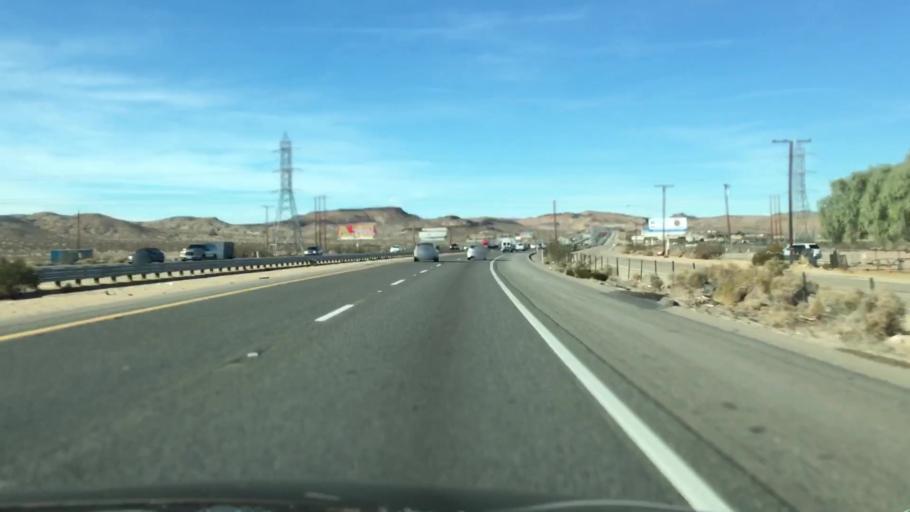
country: US
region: California
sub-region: San Bernardino County
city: Barstow
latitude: 34.9015
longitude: -116.8964
